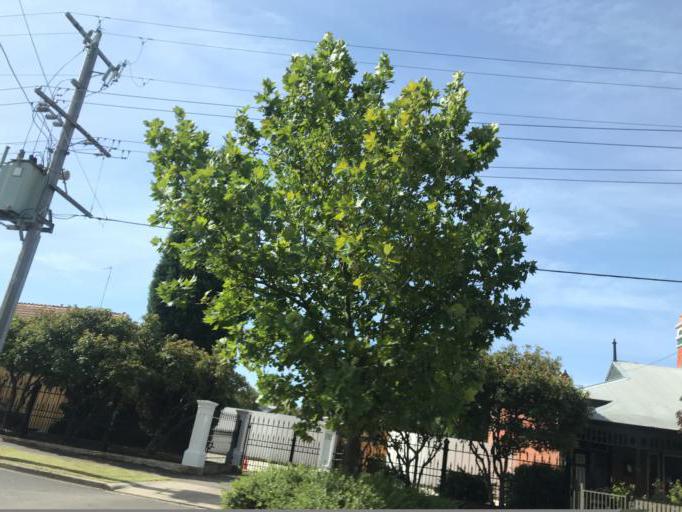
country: AU
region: Victoria
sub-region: Ballarat North
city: Ballarat Central
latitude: -37.5588
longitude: 143.8501
